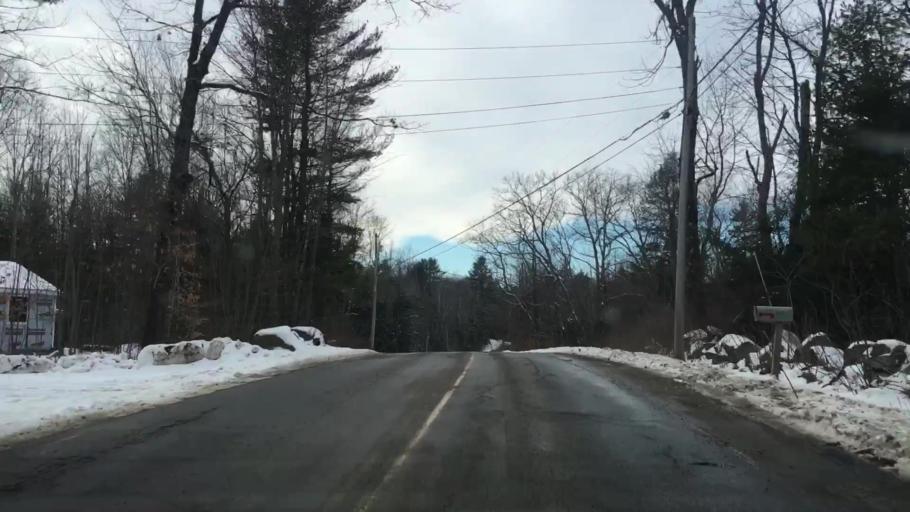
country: US
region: Maine
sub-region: Kennebec County
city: Chelsea
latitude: 44.2513
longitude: -69.7226
